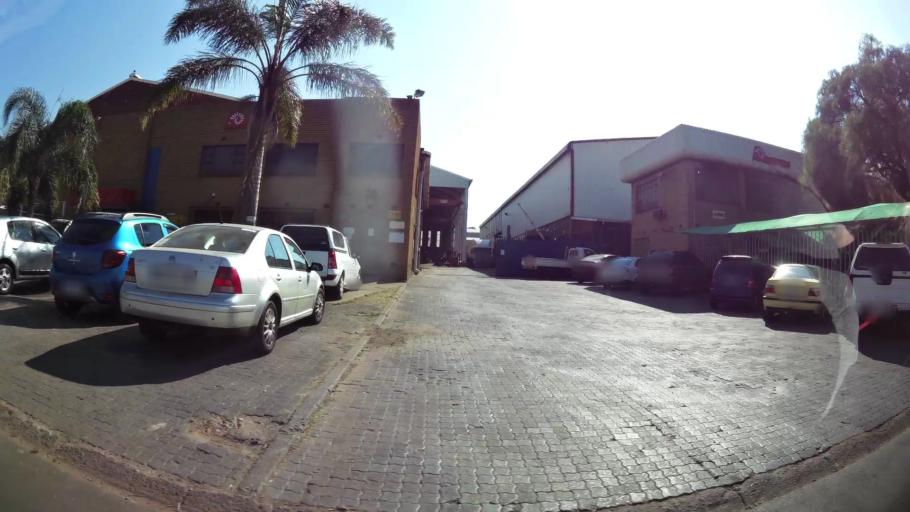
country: ZA
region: Gauteng
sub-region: Ekurhuleni Metropolitan Municipality
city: Boksburg
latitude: -26.1575
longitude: 28.2186
